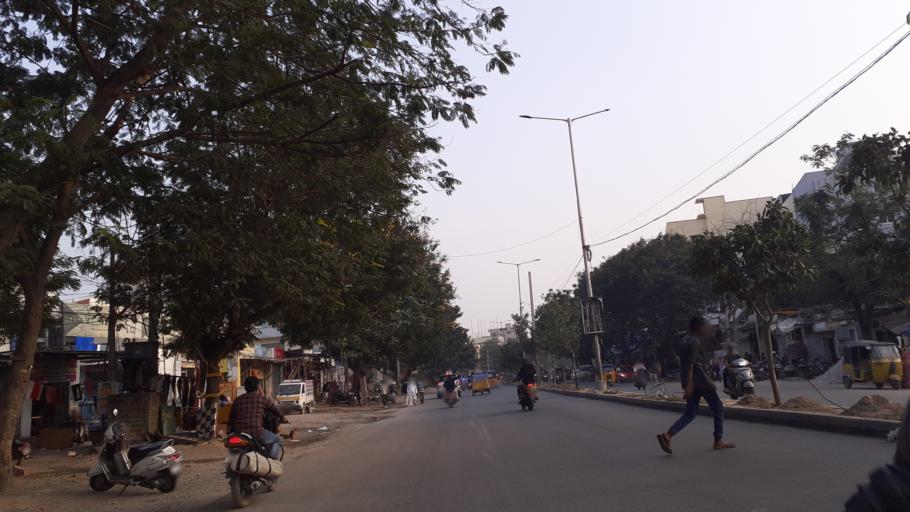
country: IN
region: Telangana
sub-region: Rangareddi
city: Kukatpalli
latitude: 17.4779
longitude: 78.3622
